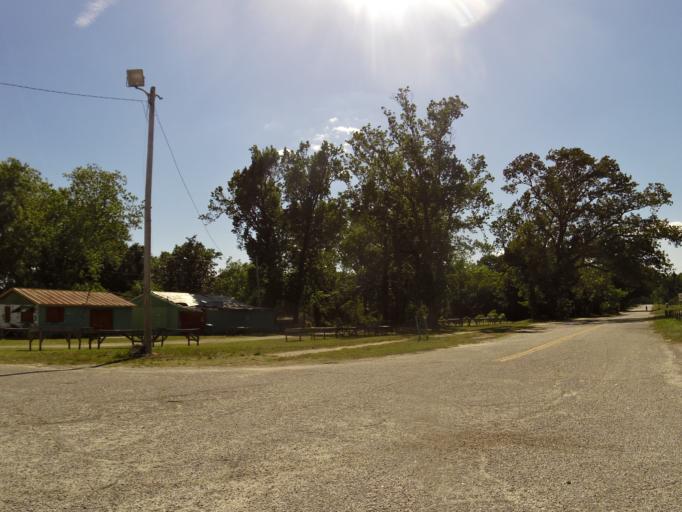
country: US
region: South Carolina
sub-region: Bamberg County
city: Denmark
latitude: 33.3261
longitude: -81.1436
